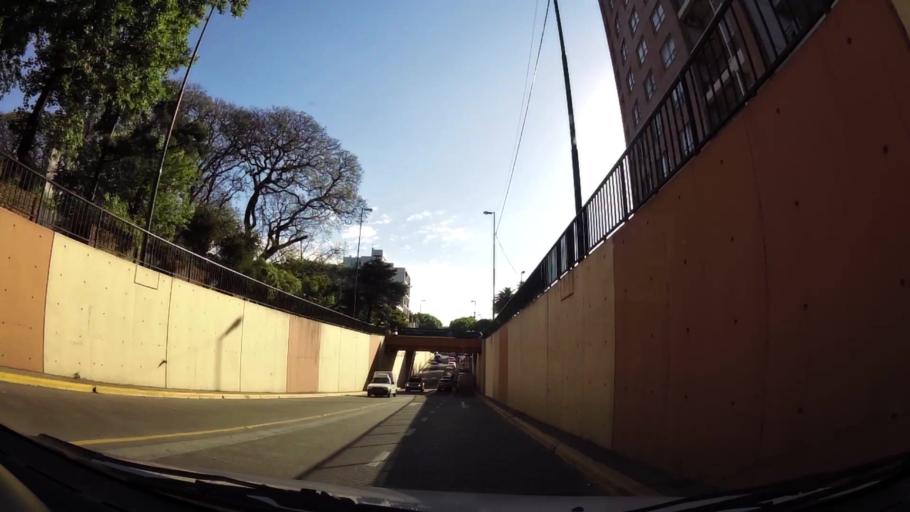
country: AR
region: Buenos Aires
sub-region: Partido de San Isidro
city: San Isidro
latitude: -34.4735
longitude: -58.5111
